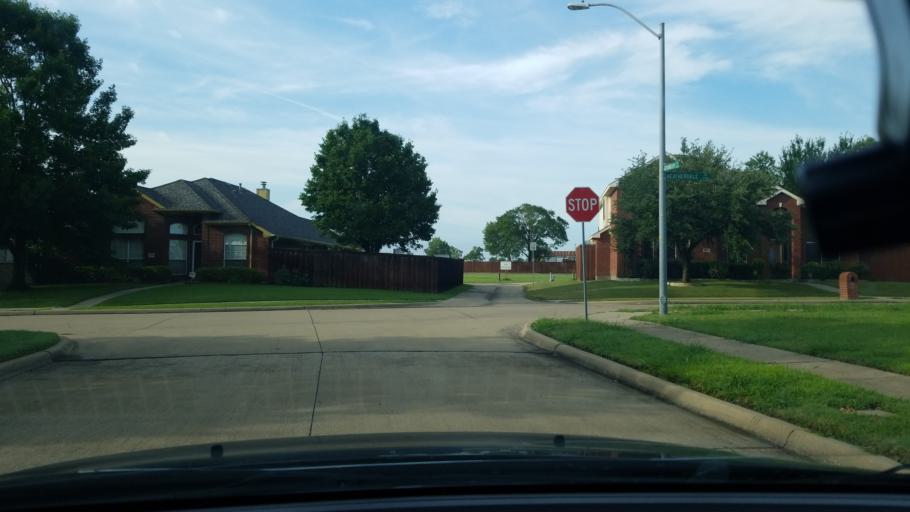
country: US
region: Texas
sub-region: Dallas County
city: Mesquite
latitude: 32.7954
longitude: -96.6039
